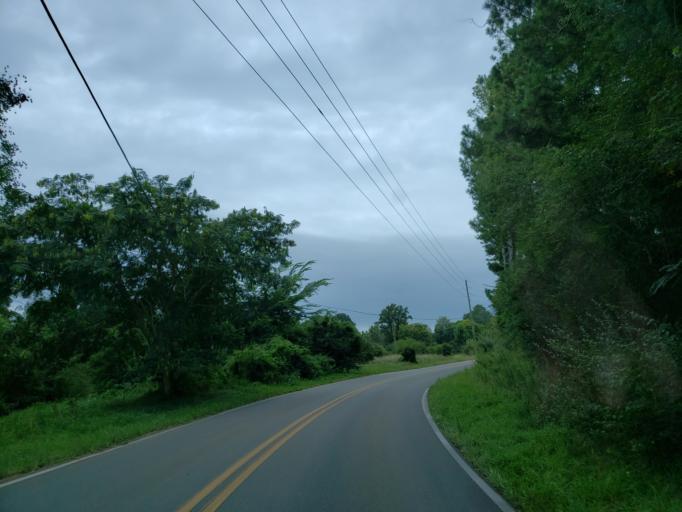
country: US
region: Georgia
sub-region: Pickens County
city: Jasper
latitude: 34.4187
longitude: -84.5753
